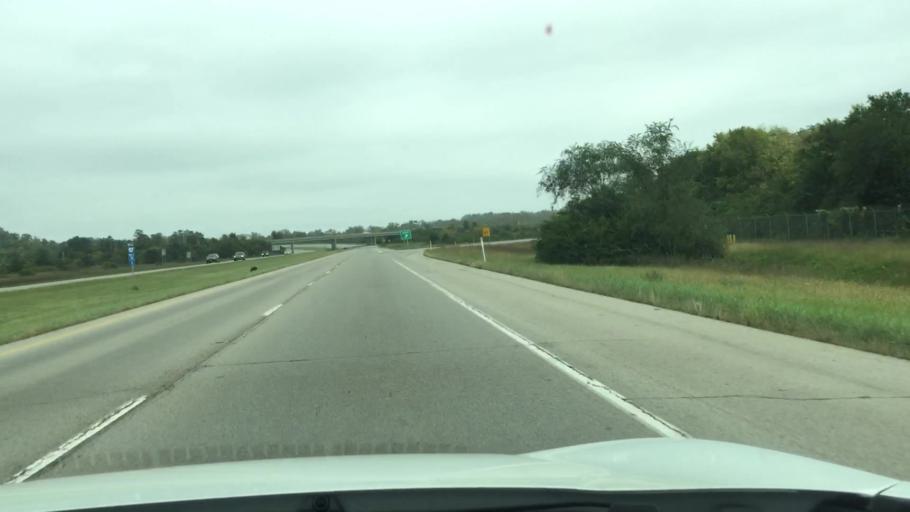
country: US
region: Ohio
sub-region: Montgomery County
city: Riverside
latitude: 39.8015
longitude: -84.1092
